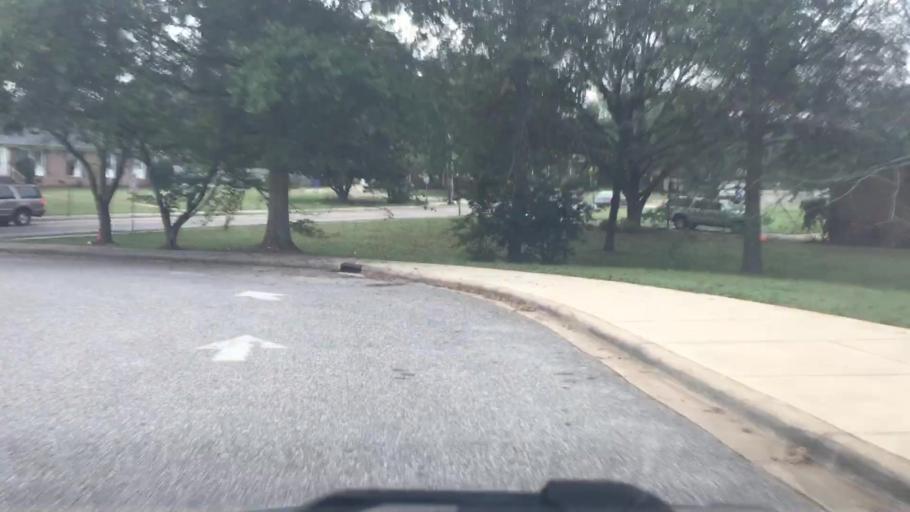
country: US
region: North Carolina
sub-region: Iredell County
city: Mooresville
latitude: 35.5620
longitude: -80.8023
